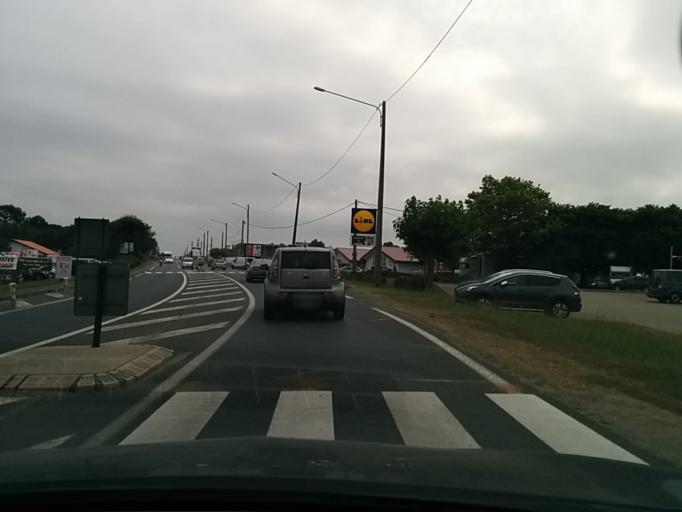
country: FR
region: Aquitaine
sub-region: Departement des Pyrenees-Atlantiques
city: Bidart
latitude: 43.4474
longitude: -1.5742
